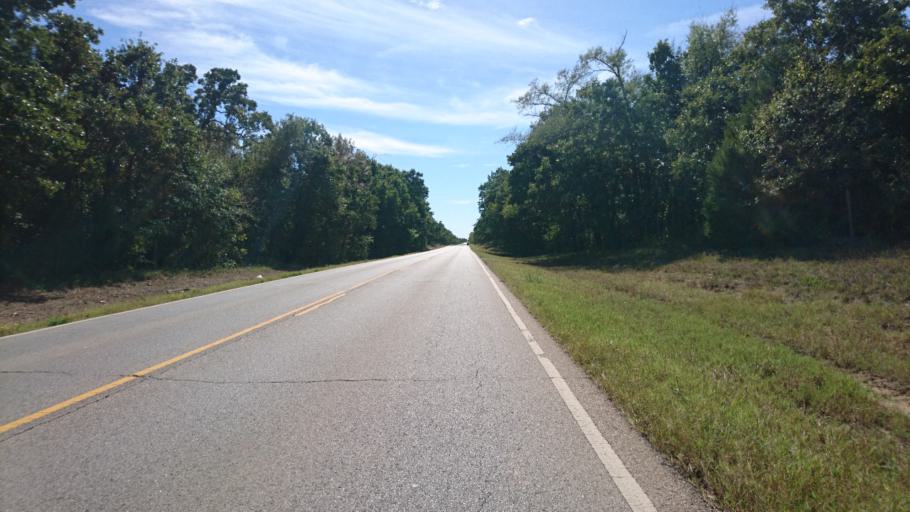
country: US
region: Oklahoma
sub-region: Lincoln County
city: Stroud
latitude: 35.7315
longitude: -96.7246
